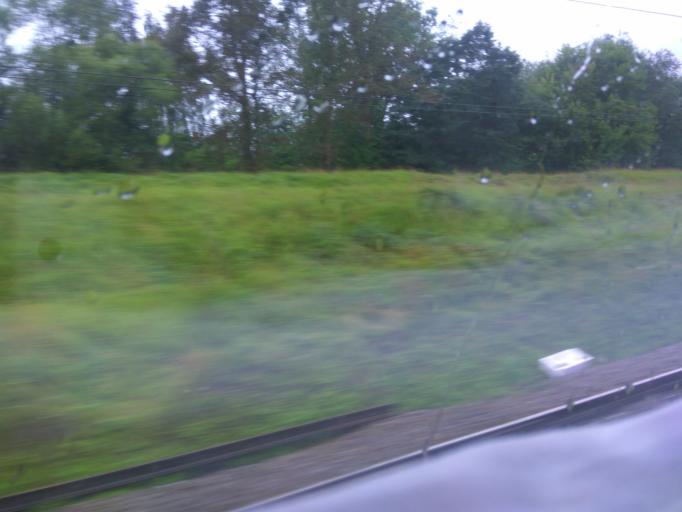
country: RU
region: Moskovskaya
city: Stupino
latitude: 54.8986
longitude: 38.0899
